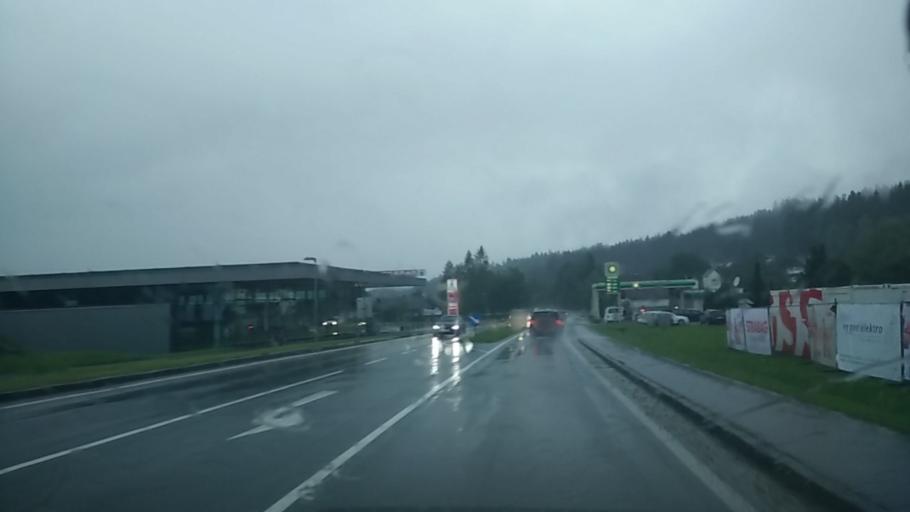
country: AT
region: Carinthia
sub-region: Politischer Bezirk Villach Land
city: Wernberg
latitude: 46.6236
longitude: 13.9371
